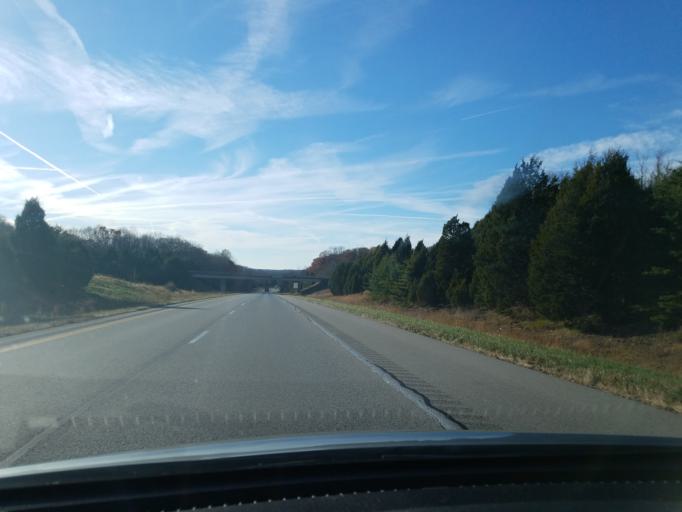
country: US
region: Indiana
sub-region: Harrison County
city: Corydon
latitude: 38.2544
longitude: -86.2844
